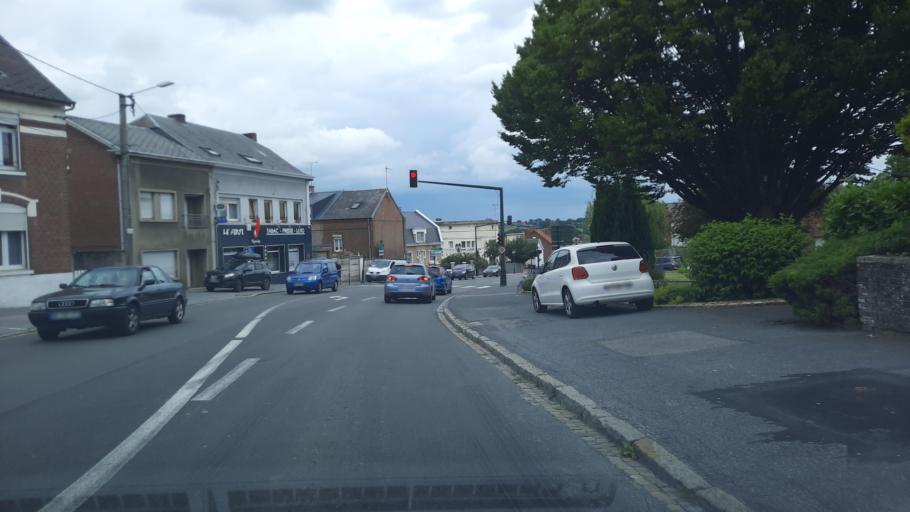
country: FR
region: Nord-Pas-de-Calais
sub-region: Departement du Nord
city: Avesnes-sur-Helpe
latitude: 50.1220
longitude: 3.9255
